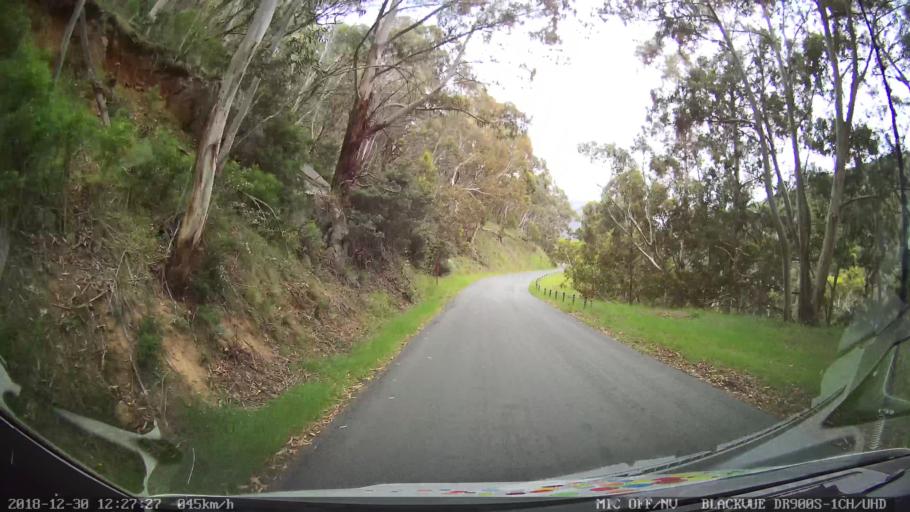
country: AU
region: New South Wales
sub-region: Snowy River
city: Jindabyne
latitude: -36.3309
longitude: 148.4901
